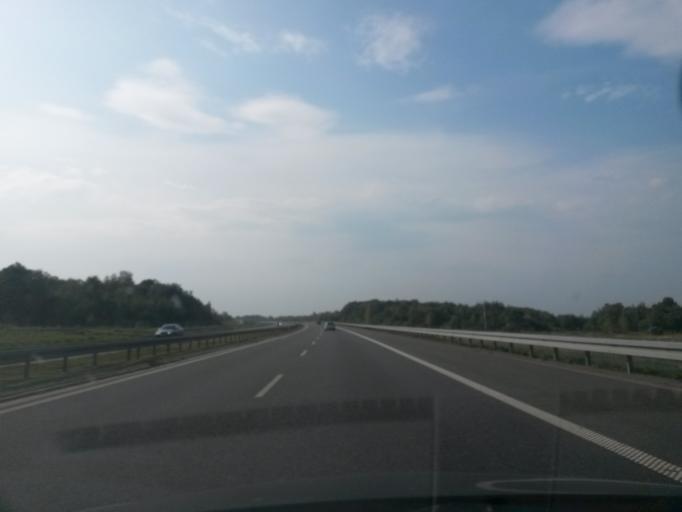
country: PL
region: Lesser Poland Voivodeship
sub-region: Powiat bochenski
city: Borek
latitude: 50.0072
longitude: 20.5356
